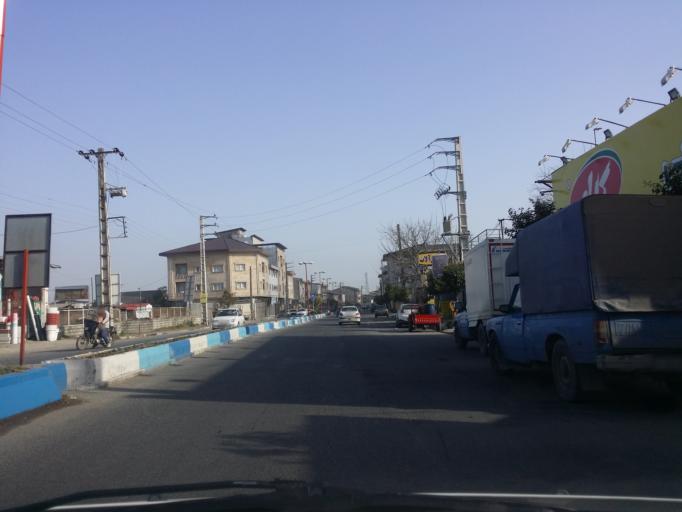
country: IR
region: Mazandaran
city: `Abbasabad
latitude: 36.7218
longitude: 51.1031
